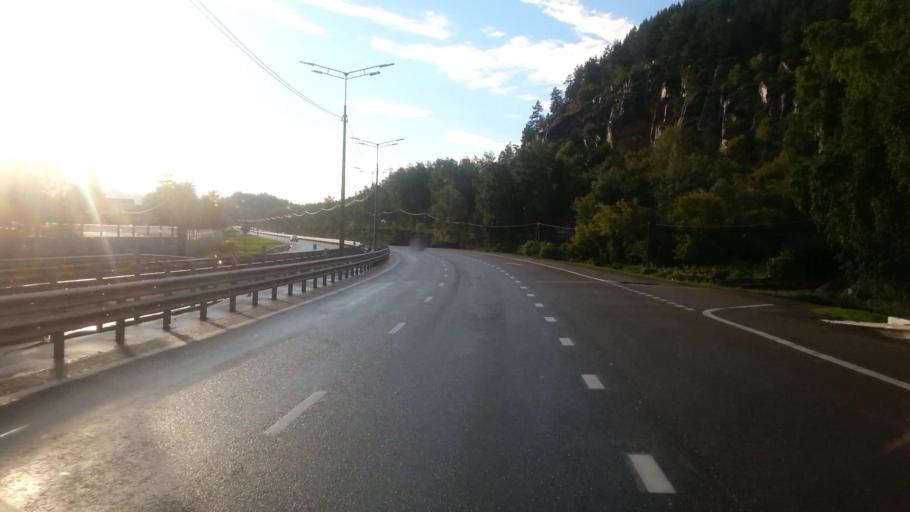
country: RU
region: Altay
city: Souzga
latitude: 51.9187
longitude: 85.8584
